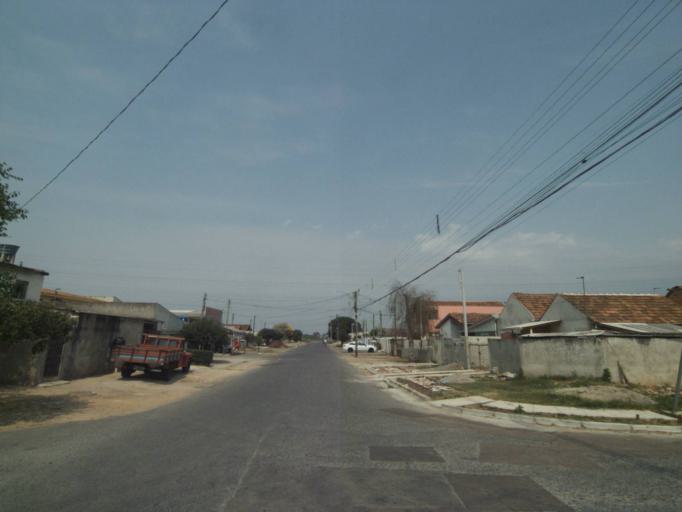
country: BR
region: Parana
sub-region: Pinhais
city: Pinhais
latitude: -25.4857
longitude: -49.1946
